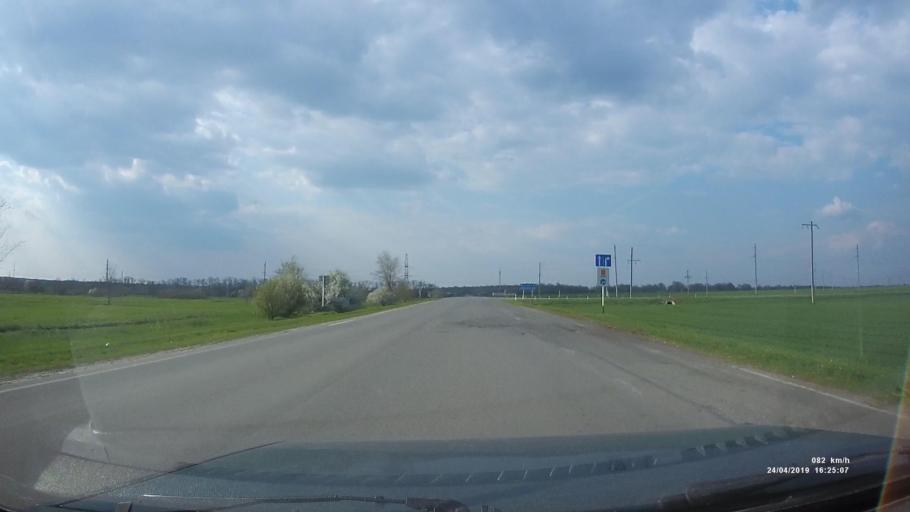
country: RU
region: Rostov
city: Orlovskiy
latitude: 46.8490
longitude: 42.0438
